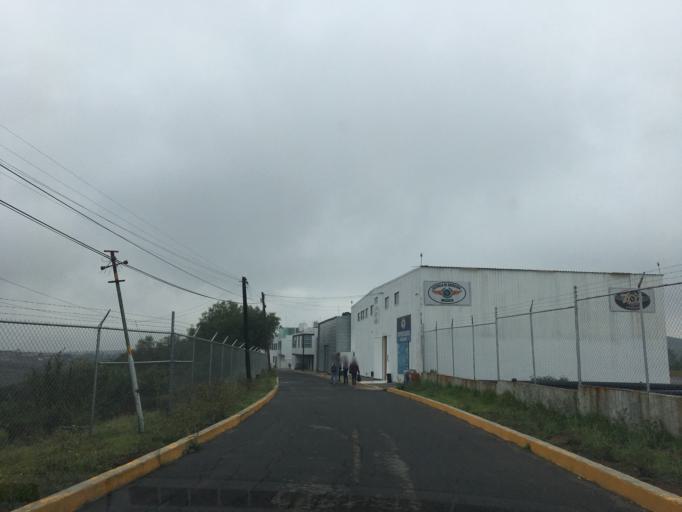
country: MX
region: Mexico
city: Ciudad Lopez Mateos
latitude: 19.5727
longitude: -99.2929
